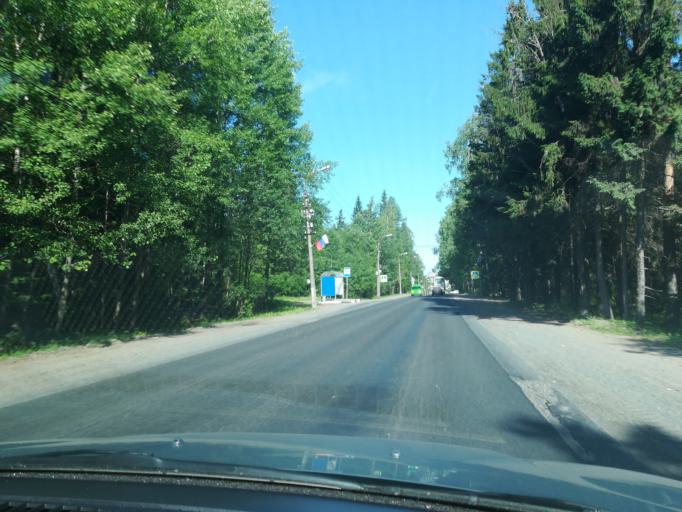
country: RU
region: Leningrad
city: Svetogorsk
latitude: 61.1029
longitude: 28.8699
